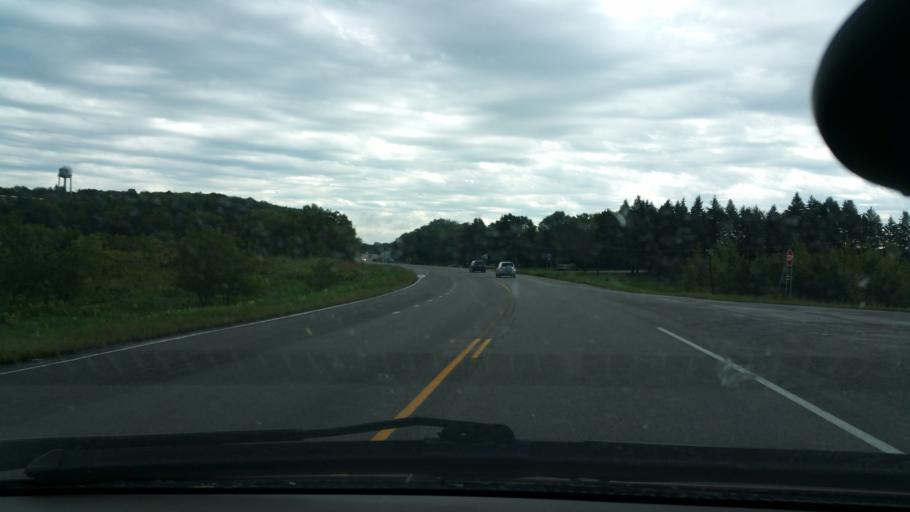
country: US
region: Minnesota
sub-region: Rice County
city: Dundas
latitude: 44.4572
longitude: -93.1948
